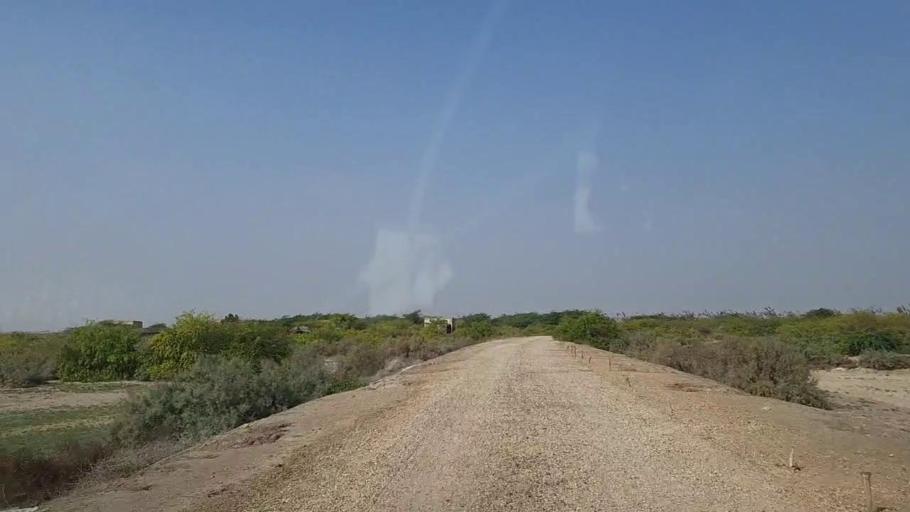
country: PK
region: Sindh
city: Mirpur Sakro
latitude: 24.6604
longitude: 67.7262
